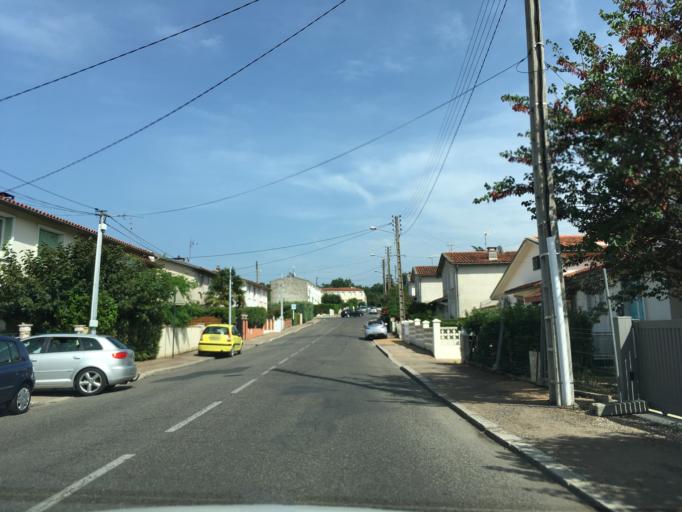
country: FR
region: Midi-Pyrenees
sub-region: Departement du Tarn
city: Castres
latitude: 43.6103
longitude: 2.2567
